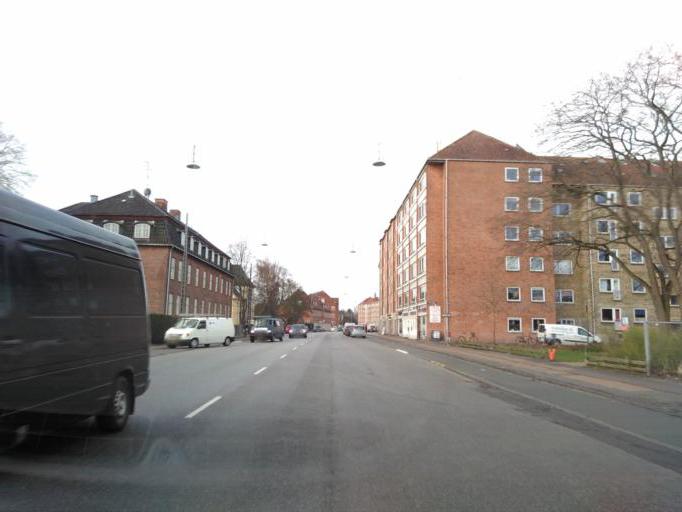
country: DK
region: Capital Region
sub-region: Kobenhavn
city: Christianshavn
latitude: 55.6562
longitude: 12.6046
